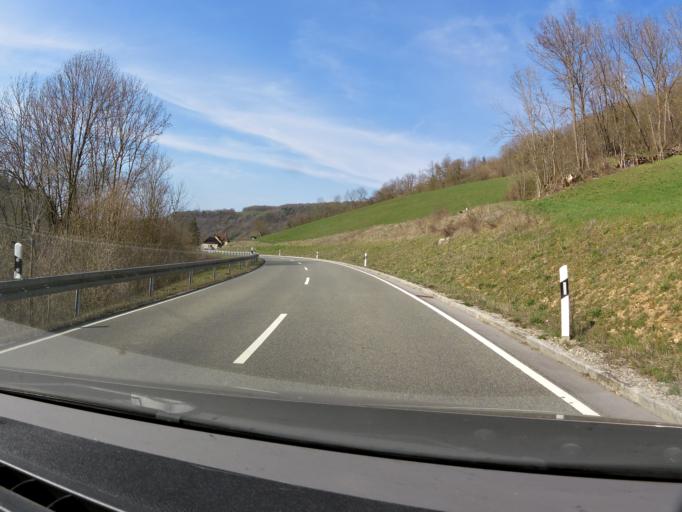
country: DE
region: Bavaria
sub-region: Regierungsbezirk Mittelfranken
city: Adelshofen
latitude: 49.4341
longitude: 10.1420
